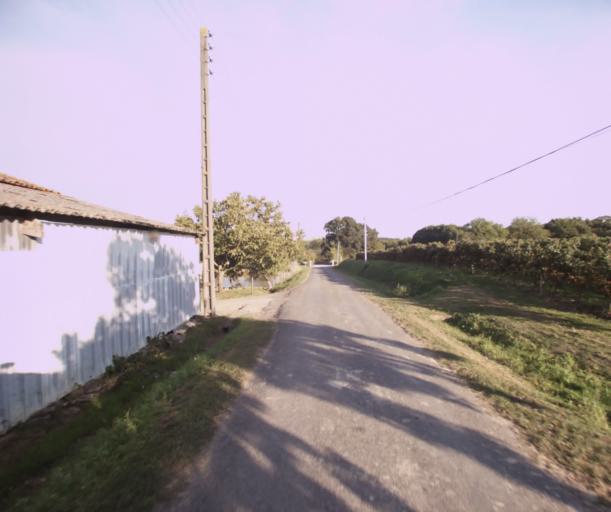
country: FR
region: Midi-Pyrenees
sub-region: Departement du Gers
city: Eauze
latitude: 43.8494
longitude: 0.0193
